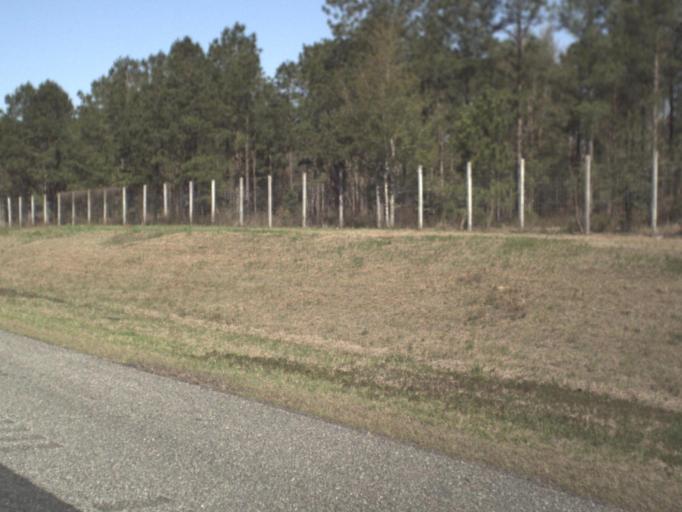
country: US
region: Florida
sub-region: Gadsden County
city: Gretna
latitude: 30.5736
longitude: -84.6836
